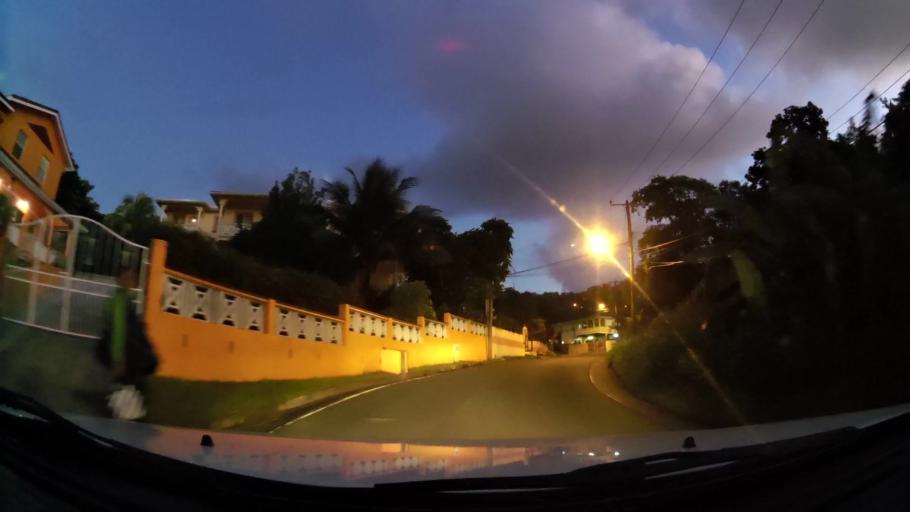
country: LC
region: Castries Quarter
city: Bisee
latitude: 14.0321
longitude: -60.9460
